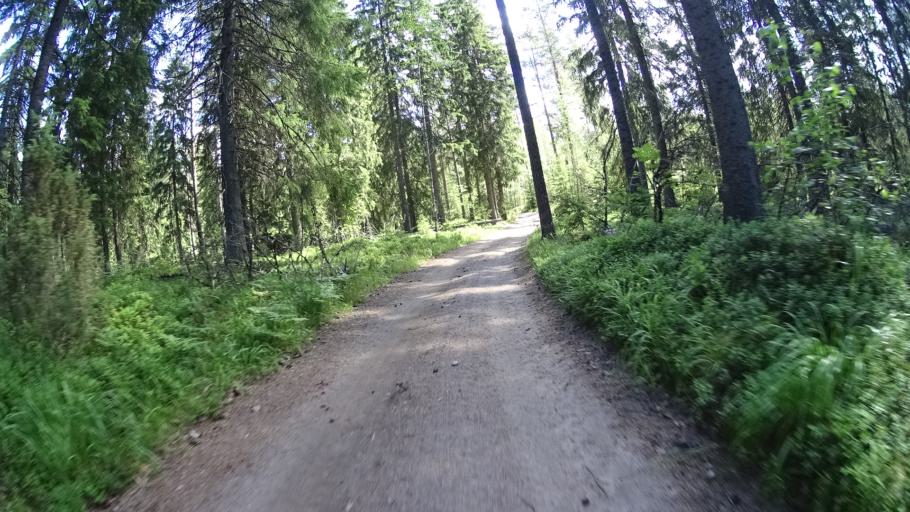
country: FI
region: Uusimaa
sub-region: Helsinki
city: Vihti
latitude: 60.3300
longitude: 24.4700
